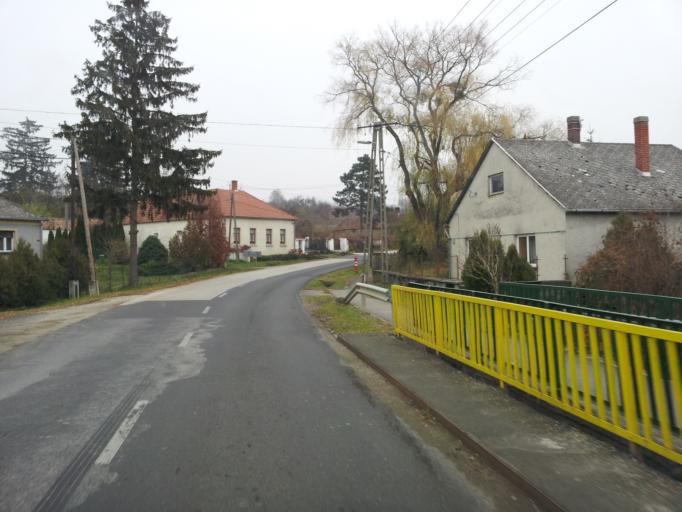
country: HU
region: Veszprem
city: Sumeg
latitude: 46.9287
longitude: 17.2453
